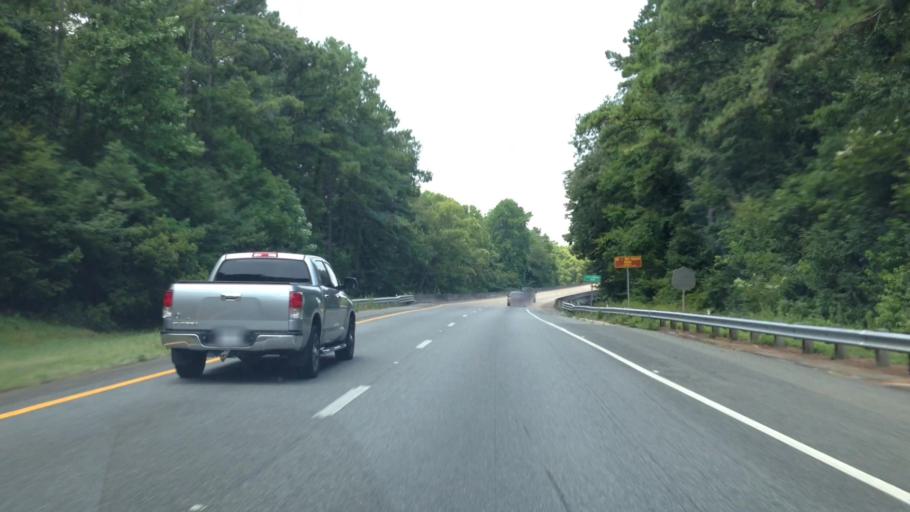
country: US
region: Florida
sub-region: Jackson County
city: Sneads
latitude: 30.6315
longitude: -84.8928
